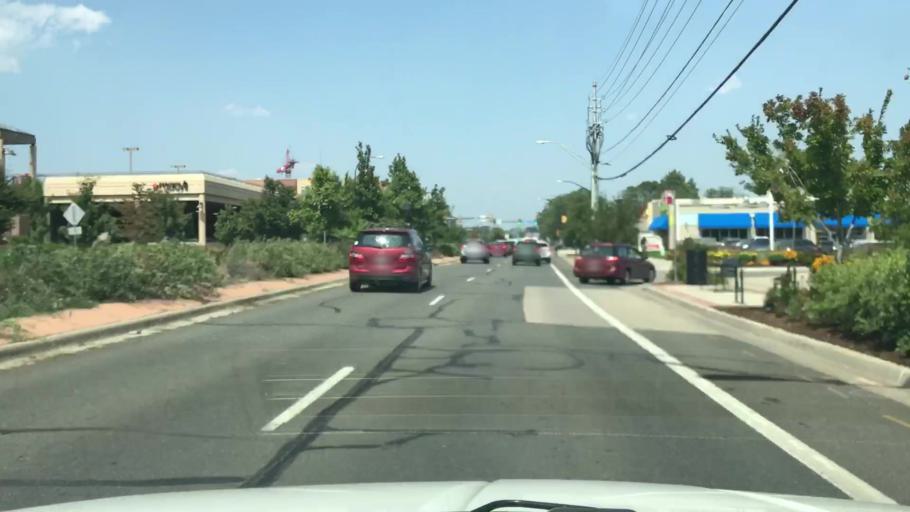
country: US
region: Colorado
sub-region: Boulder County
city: Boulder
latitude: 40.0185
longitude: -105.2536
